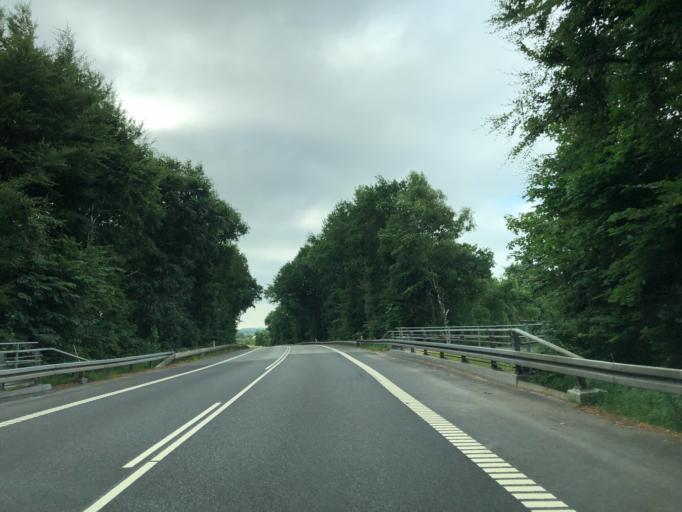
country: DK
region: South Denmark
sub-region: Vejle Kommune
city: Give
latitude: 55.8673
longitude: 9.2417
